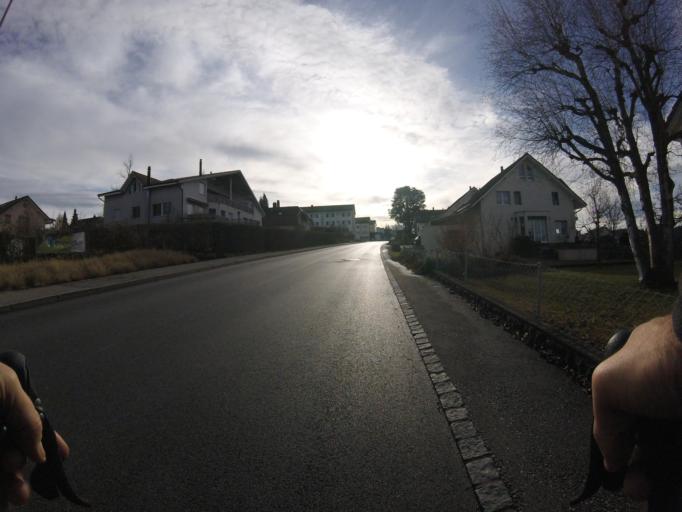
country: CH
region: Fribourg
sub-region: Sense District
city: Ueberstorf
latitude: 46.8635
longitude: 7.3124
